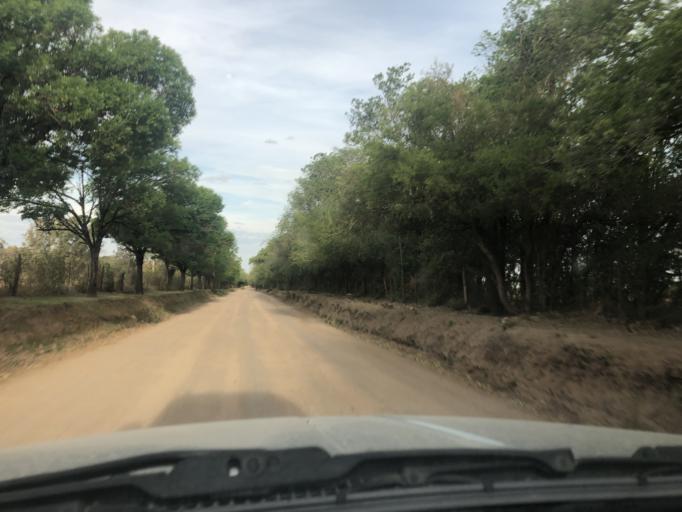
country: AR
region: Cordoba
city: La Granja
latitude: -31.0175
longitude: -64.2487
